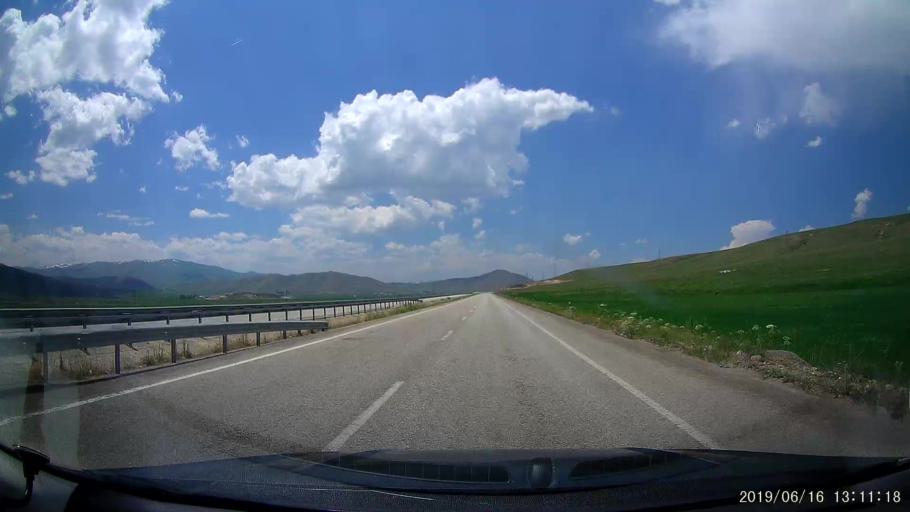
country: TR
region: Agri
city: Diyadin
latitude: 39.5913
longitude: 43.6114
